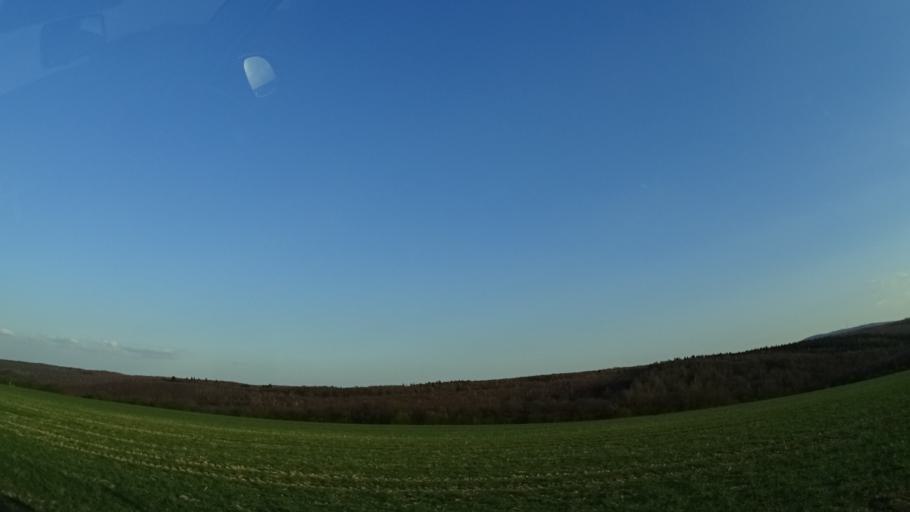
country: DE
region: Rheinland-Pfalz
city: Kriegsfeld
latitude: 49.7155
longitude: 7.9368
